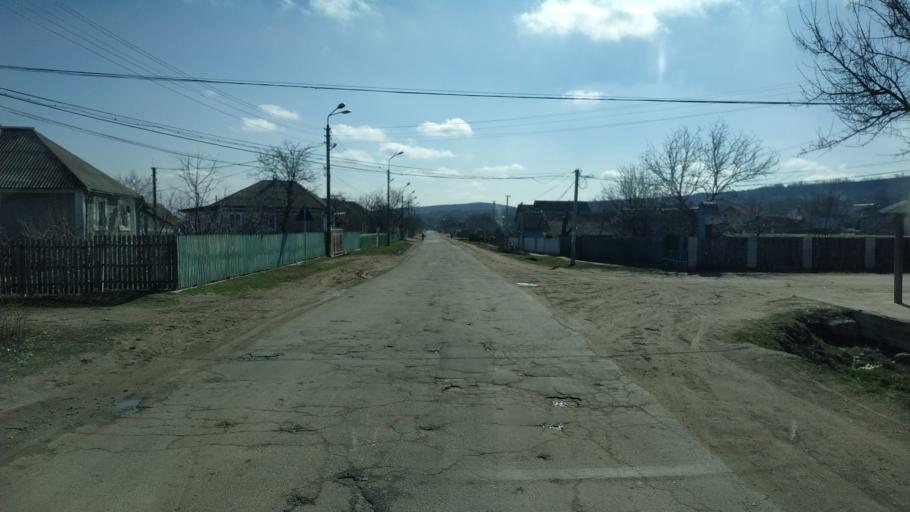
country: MD
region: Hincesti
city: Hincesti
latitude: 46.9602
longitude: 28.6033
